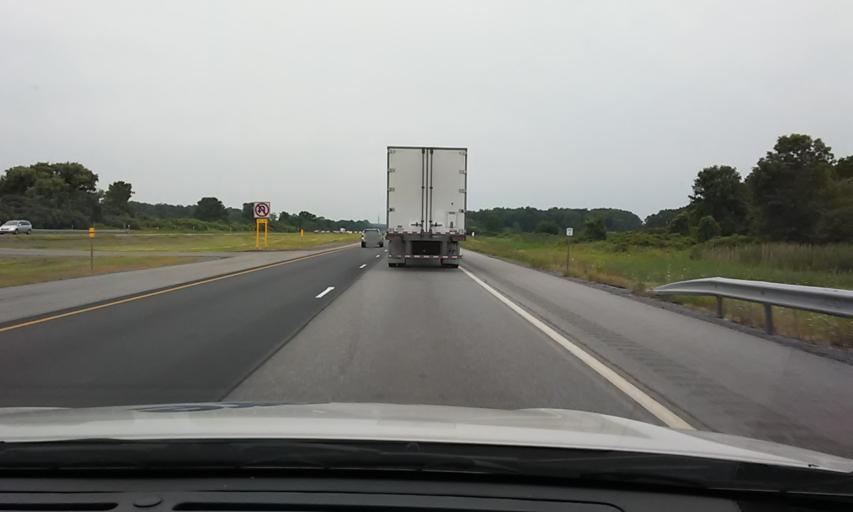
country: US
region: New York
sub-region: Genesee County
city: Le Roy
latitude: 43.0230
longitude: -78.0660
